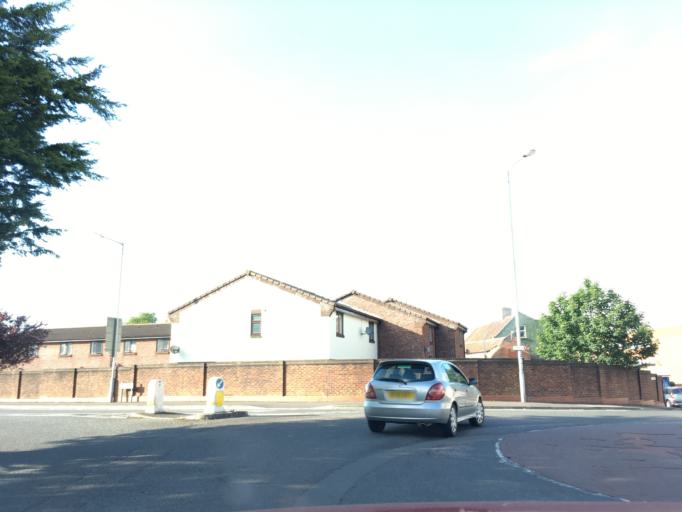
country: GB
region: England
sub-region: Somerset
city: Highbridge
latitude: 51.2196
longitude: -2.9766
